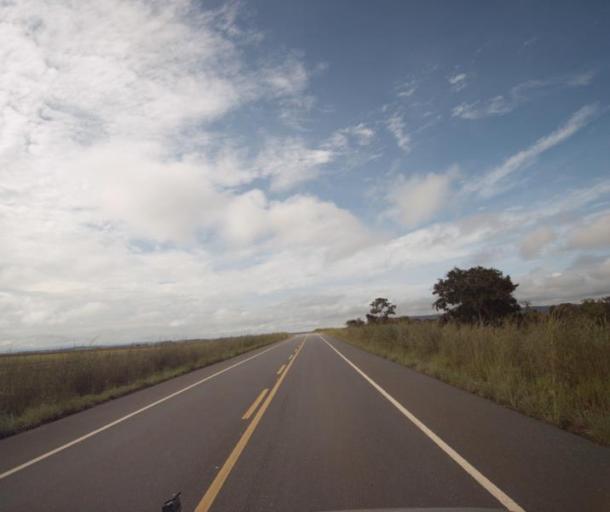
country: BR
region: Goias
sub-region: Barro Alto
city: Barro Alto
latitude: -15.2902
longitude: -48.6780
